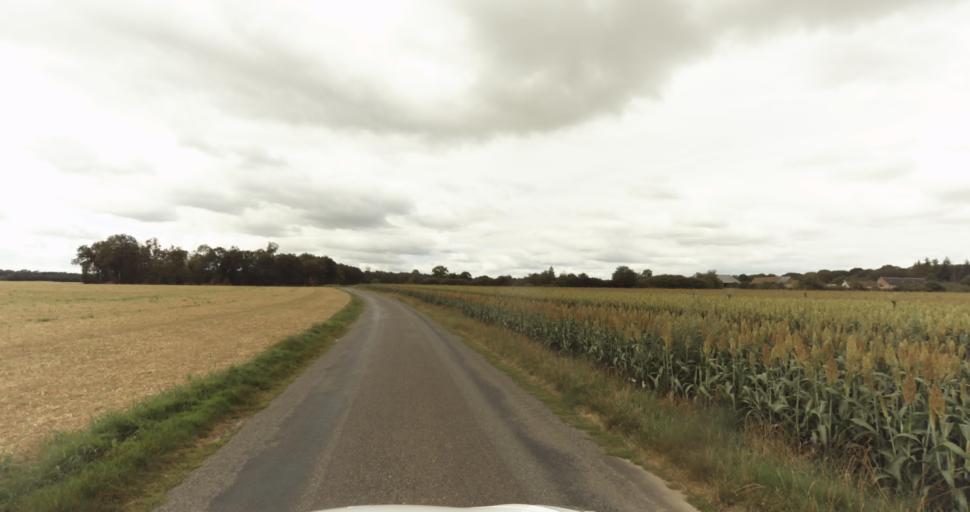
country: FR
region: Haute-Normandie
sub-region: Departement de l'Eure
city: Tillieres-sur-Avre
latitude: 48.8016
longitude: 1.1196
